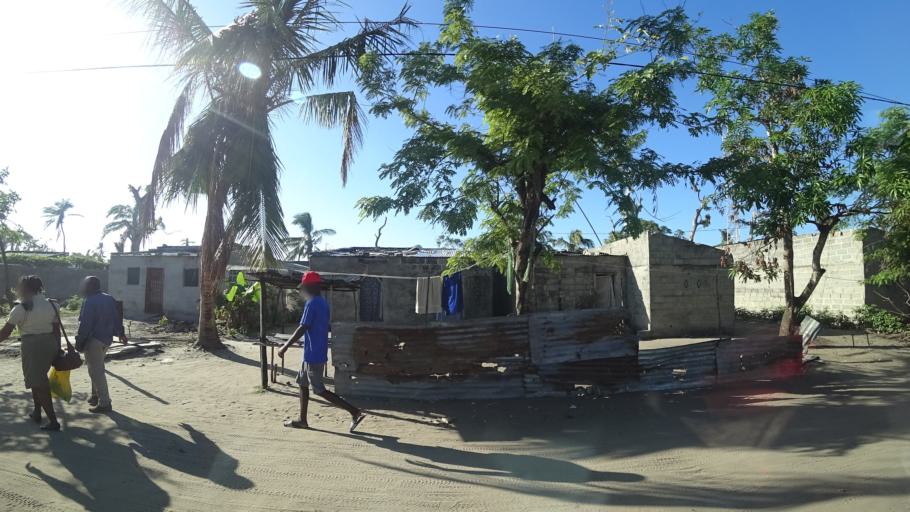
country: MZ
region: Sofala
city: Beira
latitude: -19.7730
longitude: 34.8856
